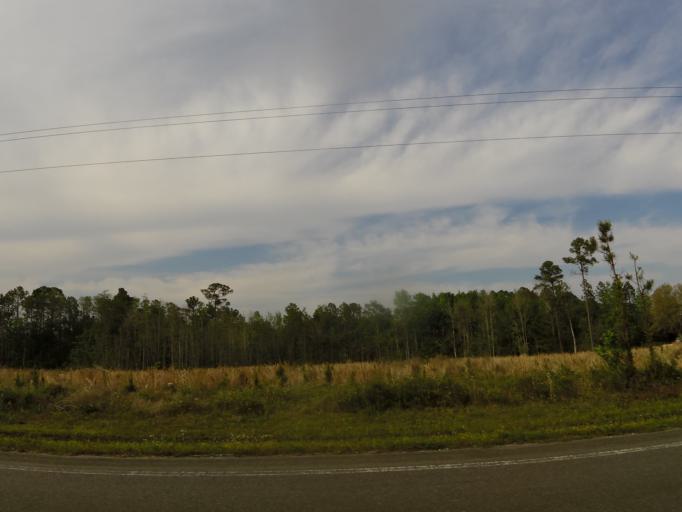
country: US
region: Florida
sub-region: Nassau County
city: Yulee
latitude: 30.6870
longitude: -81.6614
